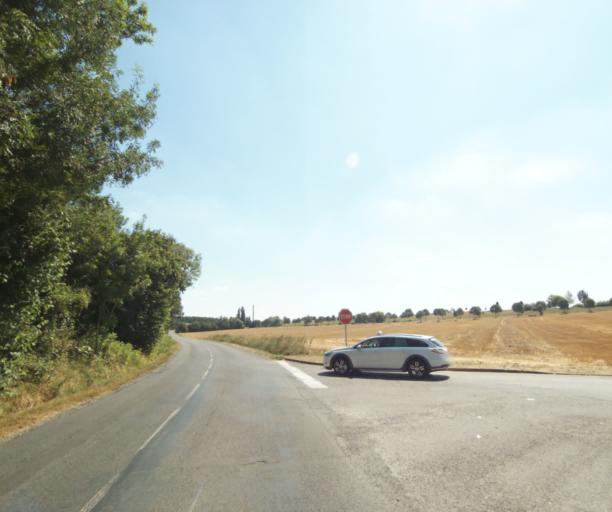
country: FR
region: Ile-de-France
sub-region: Departement de Seine-et-Marne
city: Chanteloup-en-Brie
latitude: 48.8538
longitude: 2.7305
